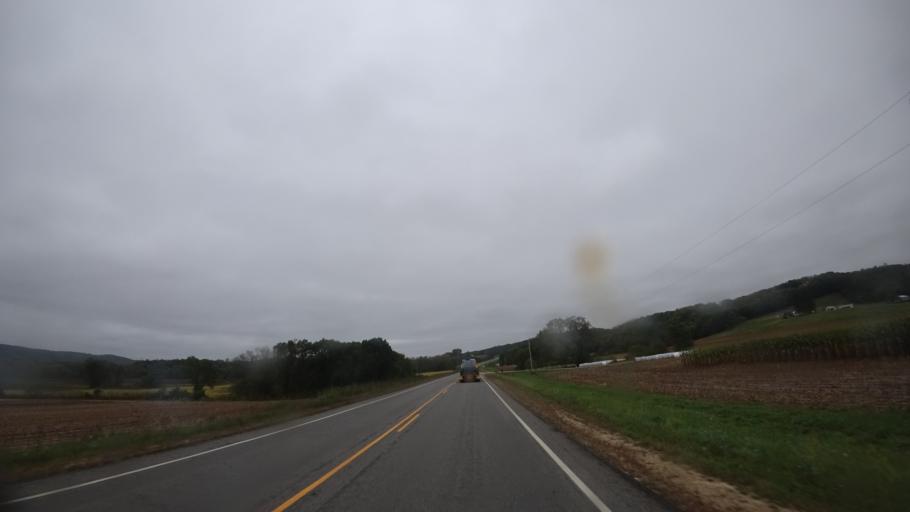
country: US
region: Wisconsin
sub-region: Crawford County
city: Prairie du Chien
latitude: 43.0311
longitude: -90.9992
